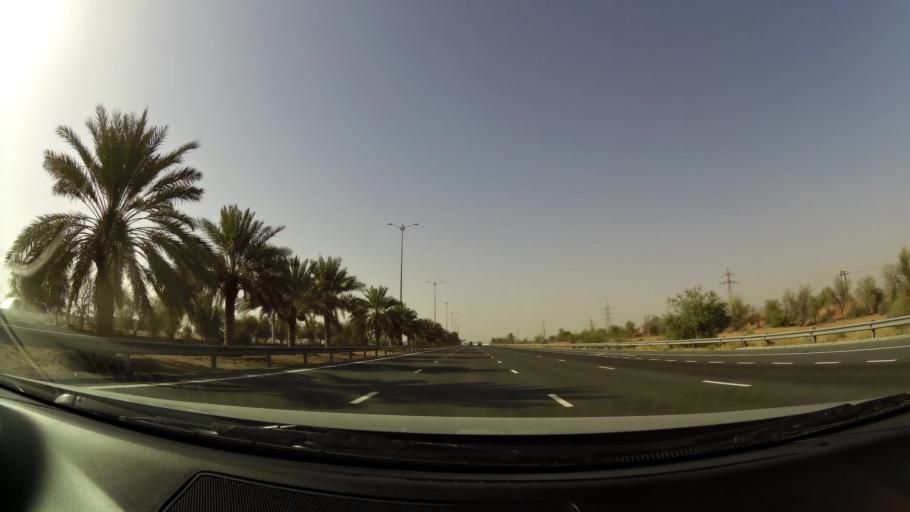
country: OM
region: Al Buraimi
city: Al Buraymi
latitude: 24.5121
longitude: 55.7647
